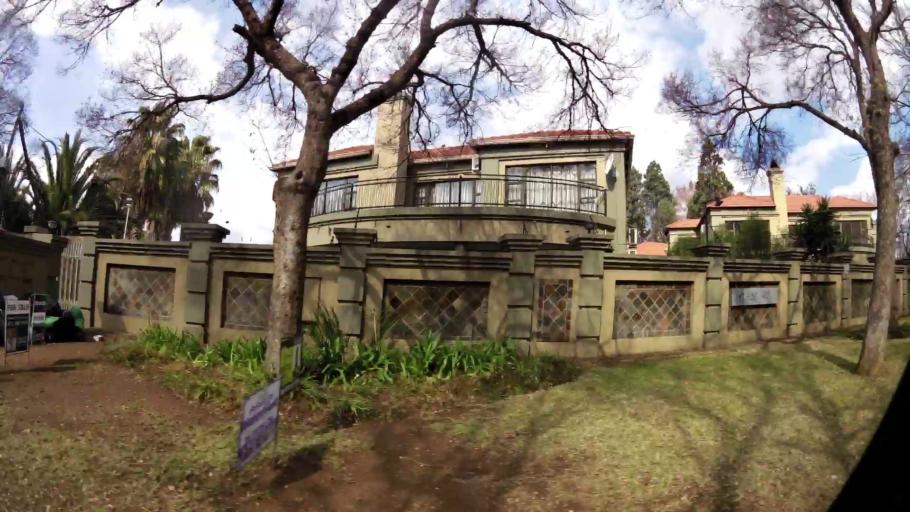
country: ZA
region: Gauteng
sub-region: Sedibeng District Municipality
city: Vanderbijlpark
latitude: -26.7409
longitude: 27.8354
